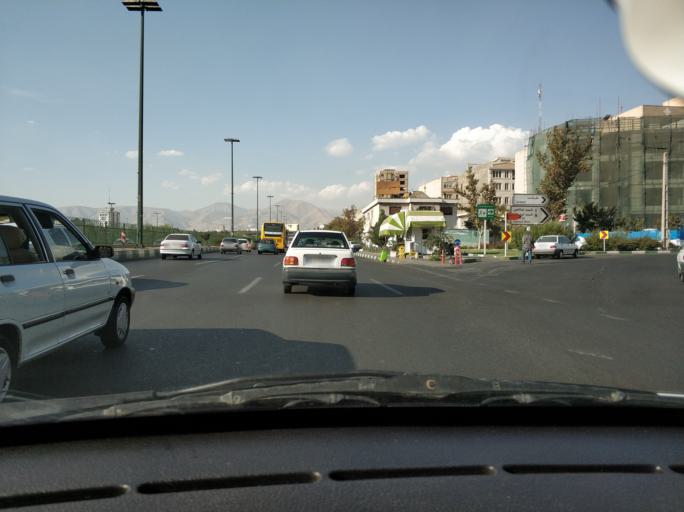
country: IR
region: Tehran
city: Tehran
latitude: 35.7059
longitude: 51.3374
